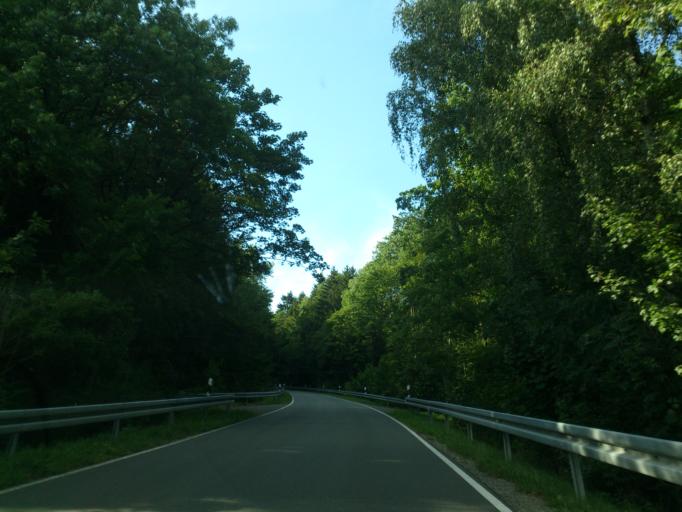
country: DE
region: North Rhine-Westphalia
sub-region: Regierungsbezirk Detmold
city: Willebadessen
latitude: 51.6639
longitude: 9.0221
